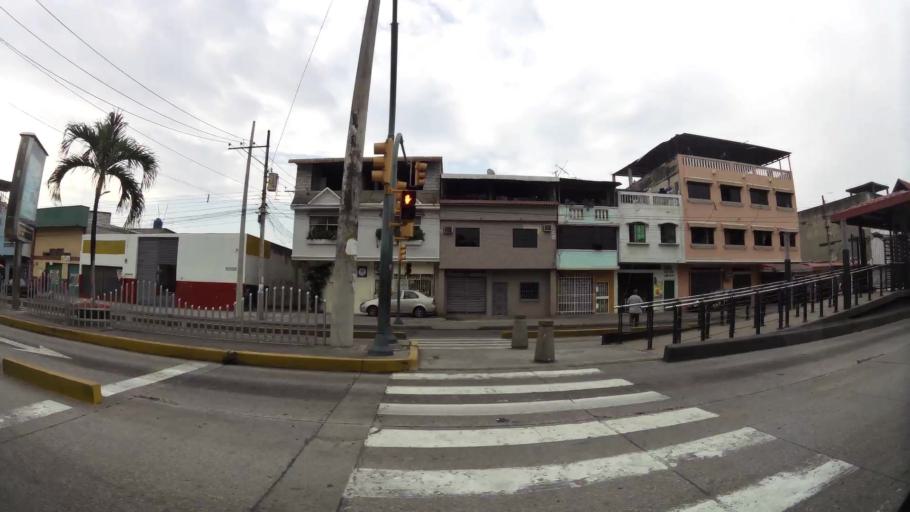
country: EC
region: Guayas
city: Guayaquil
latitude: -2.2522
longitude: -79.8825
